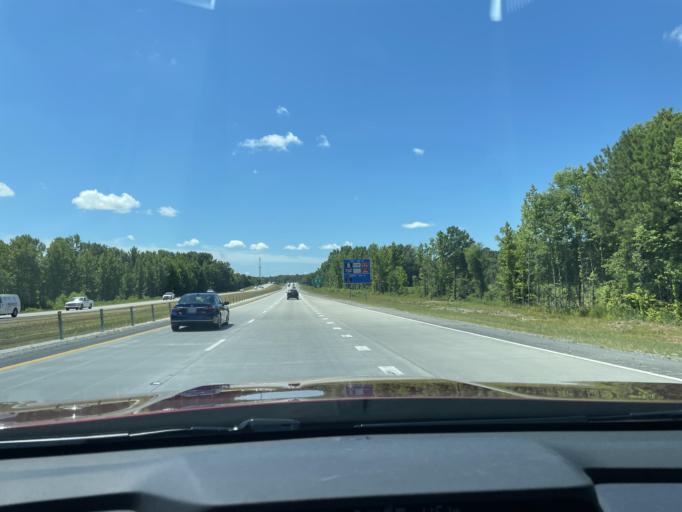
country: US
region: Arkansas
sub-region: Jefferson County
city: Sulphur Springs
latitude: 34.2116
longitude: -92.0718
